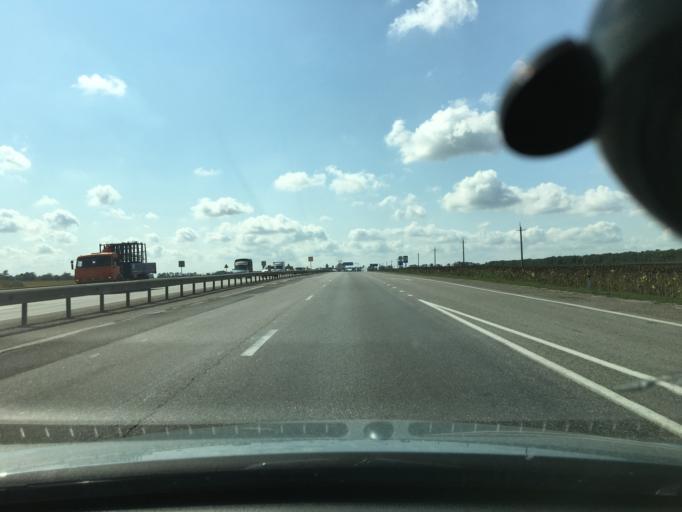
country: RU
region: Krasnodarskiy
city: Krasnoye
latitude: 46.7655
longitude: 39.6622
